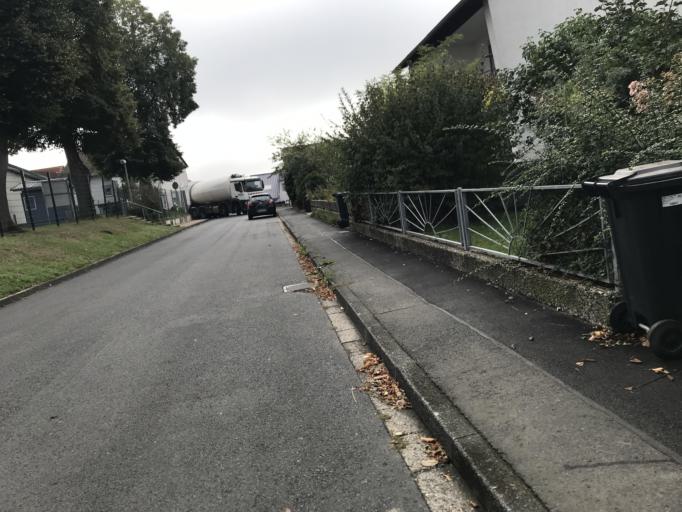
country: DE
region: Hesse
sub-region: Regierungsbezirk Kassel
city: Guxhagen
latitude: 51.2014
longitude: 9.4347
